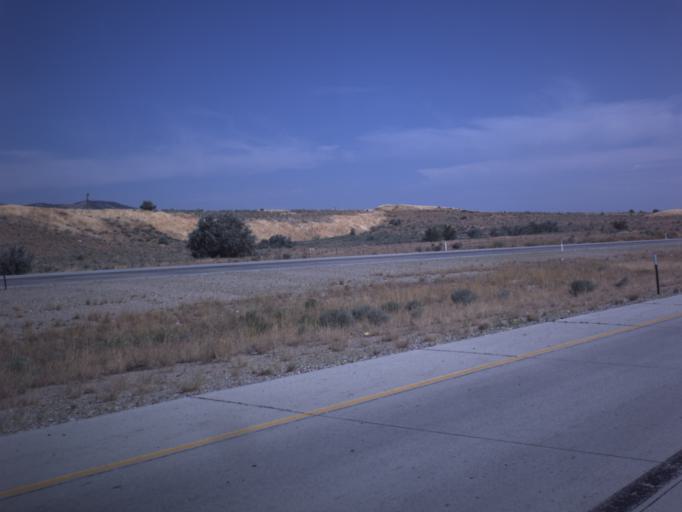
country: US
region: Utah
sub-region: Salt Lake County
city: Oquirrh
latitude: 40.6294
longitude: -112.0460
